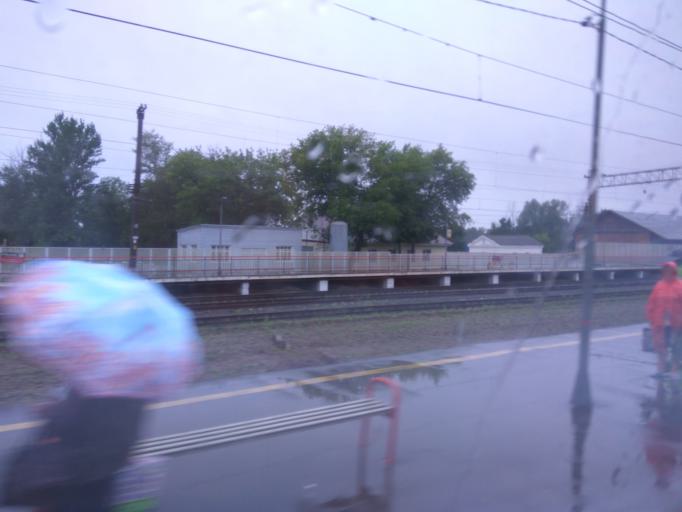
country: RU
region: Moskovskaya
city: Stupino
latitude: 54.9089
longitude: 38.0790
